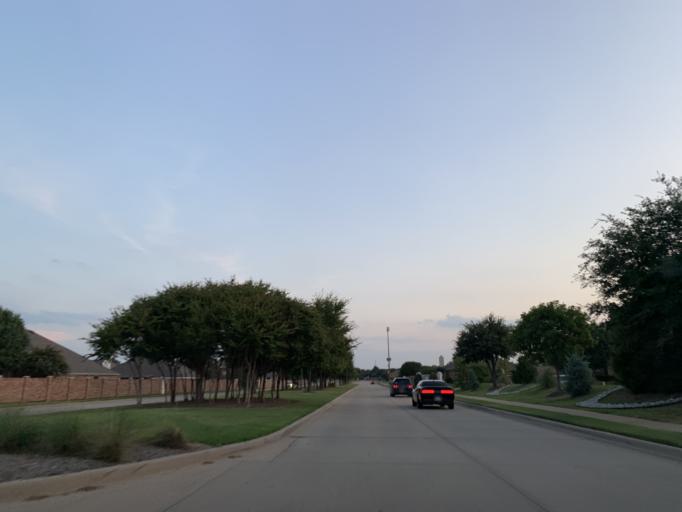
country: US
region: Texas
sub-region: Tarrant County
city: Keller
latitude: 32.9448
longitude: -97.2700
